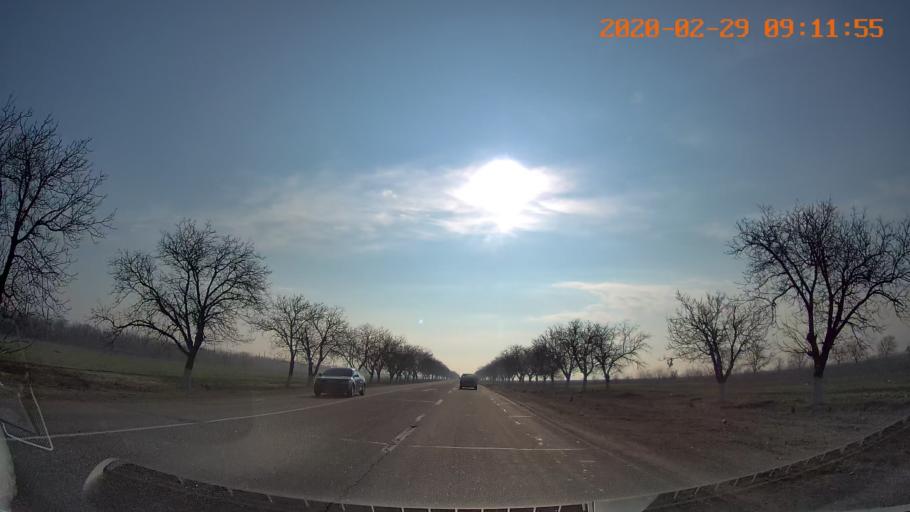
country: MD
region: Telenesti
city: Slobozia
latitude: 46.8310
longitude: 29.8081
